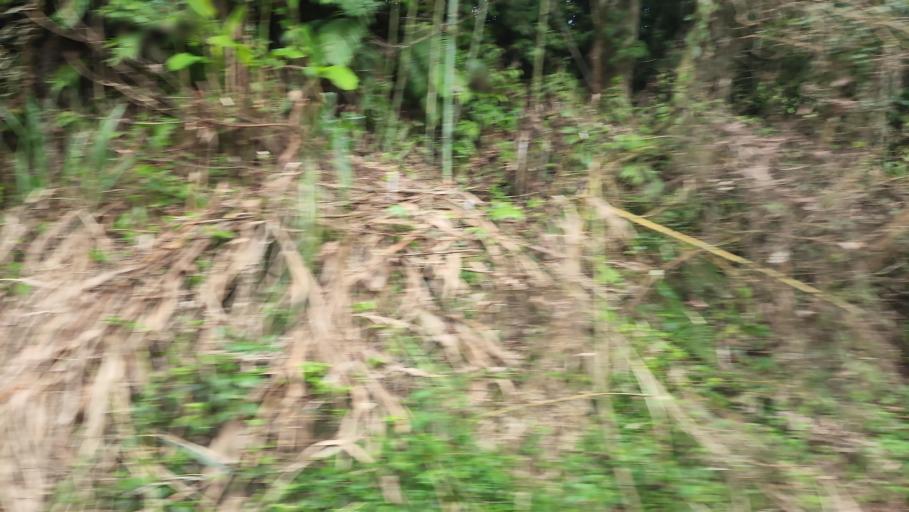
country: TW
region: Taiwan
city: Daxi
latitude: 24.8830
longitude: 121.4181
